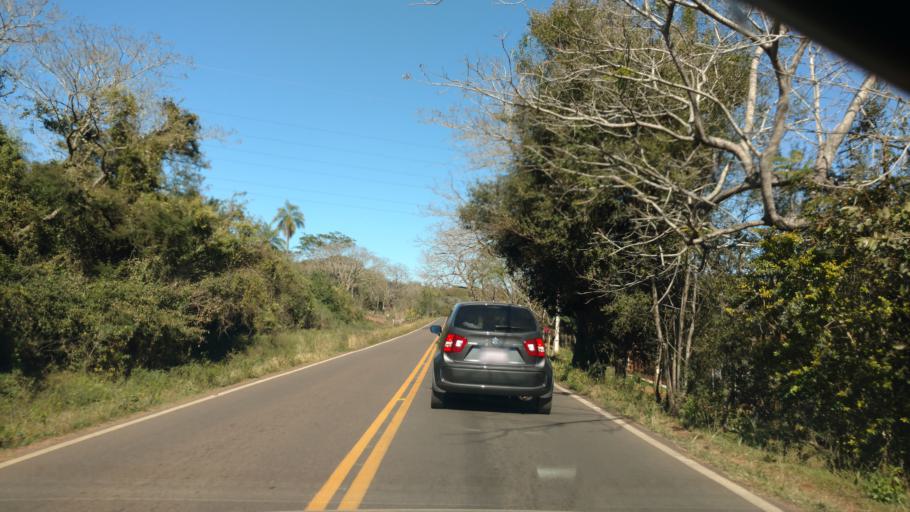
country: PY
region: Paraguari
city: Pirayu
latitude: -25.4954
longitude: -57.2456
